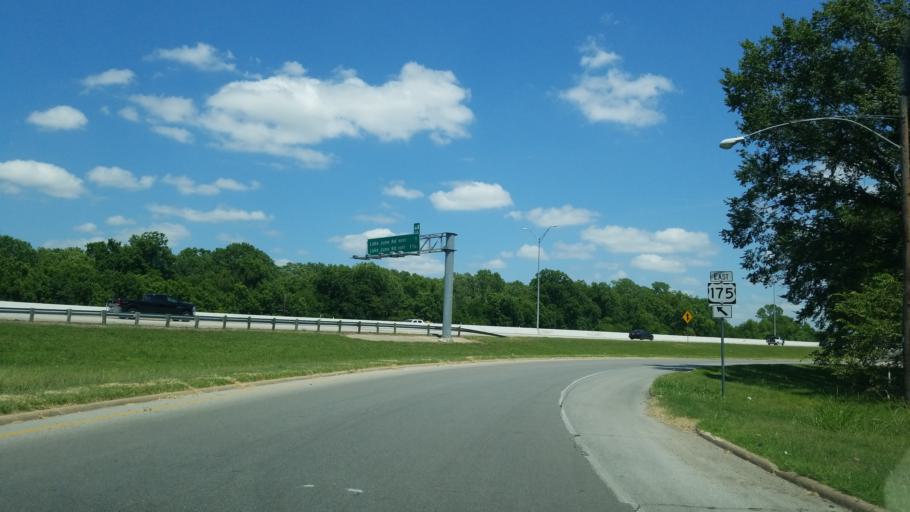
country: US
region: Texas
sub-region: Dallas County
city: Dallas
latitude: 32.7435
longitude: -96.7249
